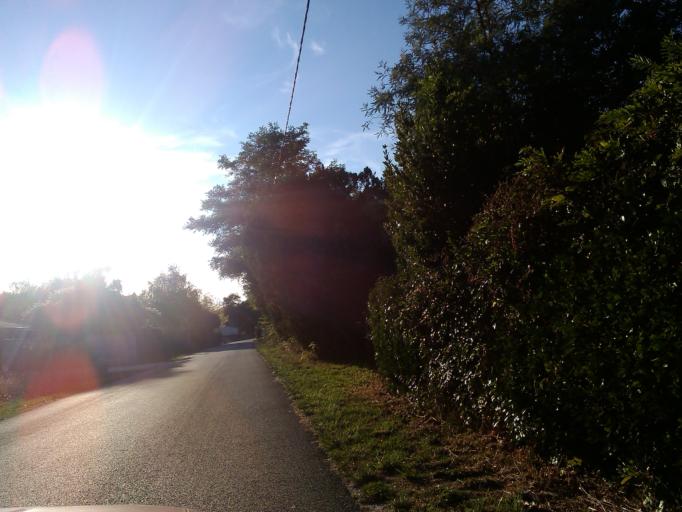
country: FR
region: Aquitaine
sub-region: Departement de la Gironde
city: Soulac-sur-Mer
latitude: 45.4328
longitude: -1.0443
